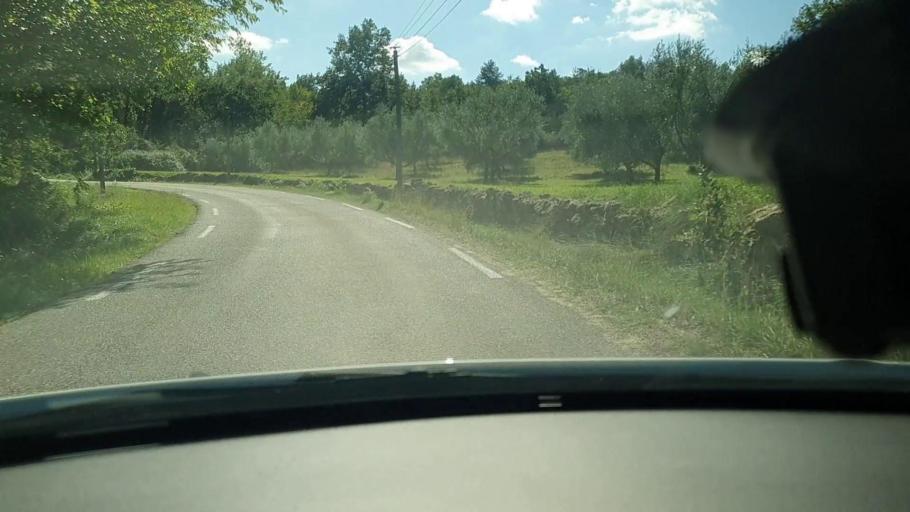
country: FR
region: Languedoc-Roussillon
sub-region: Departement du Gard
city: Goudargues
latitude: 44.1773
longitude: 4.4800
